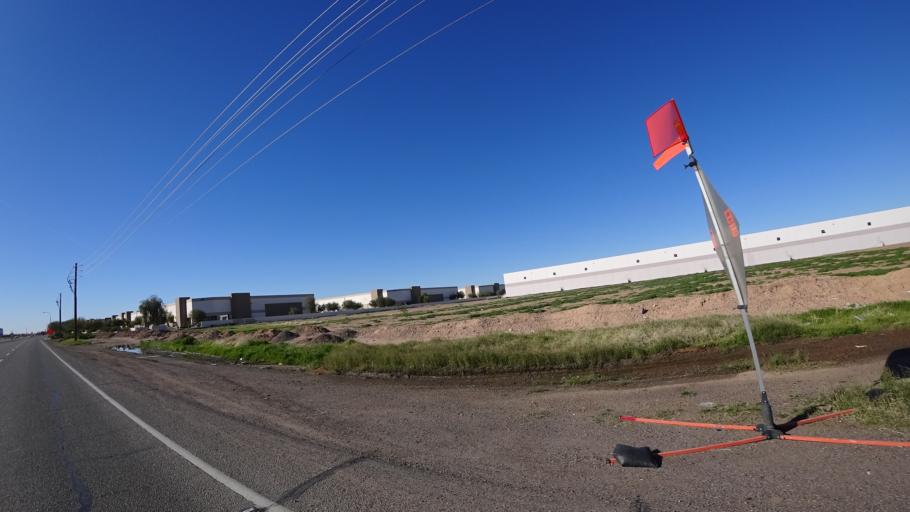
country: US
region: Arizona
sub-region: Maricopa County
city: Tolleson
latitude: 33.4371
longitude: -112.2401
